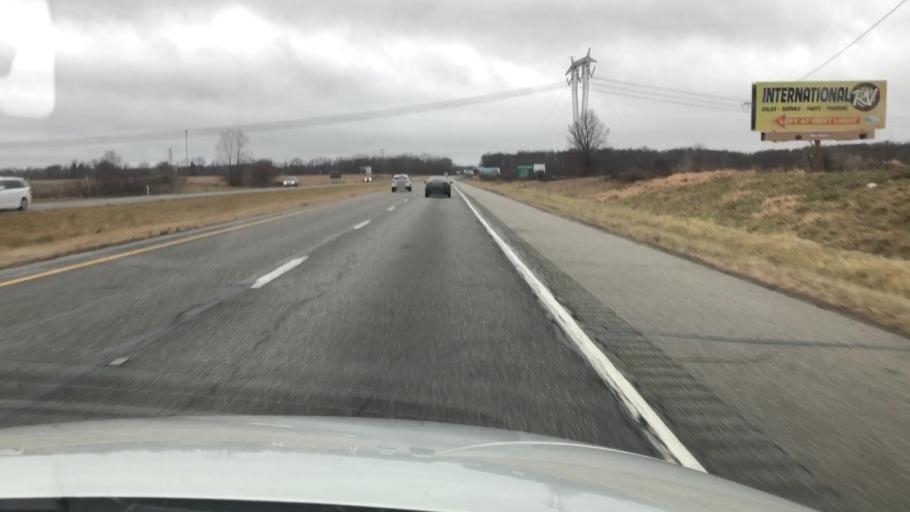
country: US
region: Indiana
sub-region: Marshall County
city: Plymouth
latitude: 41.3615
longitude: -86.3550
